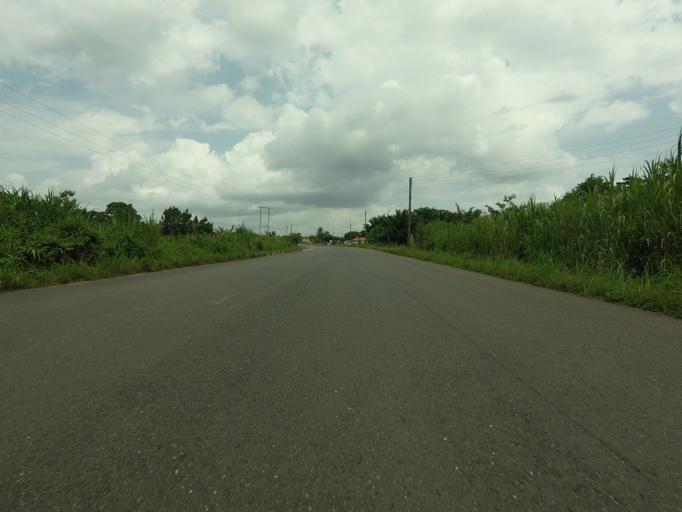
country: GH
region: Volta
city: Ho
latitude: 6.5024
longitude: 0.2066
